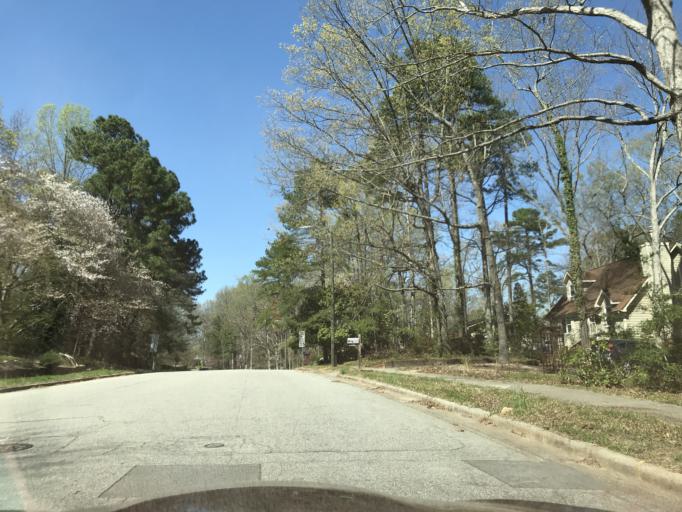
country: US
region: North Carolina
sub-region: Wake County
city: West Raleigh
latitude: 35.7756
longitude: -78.6982
